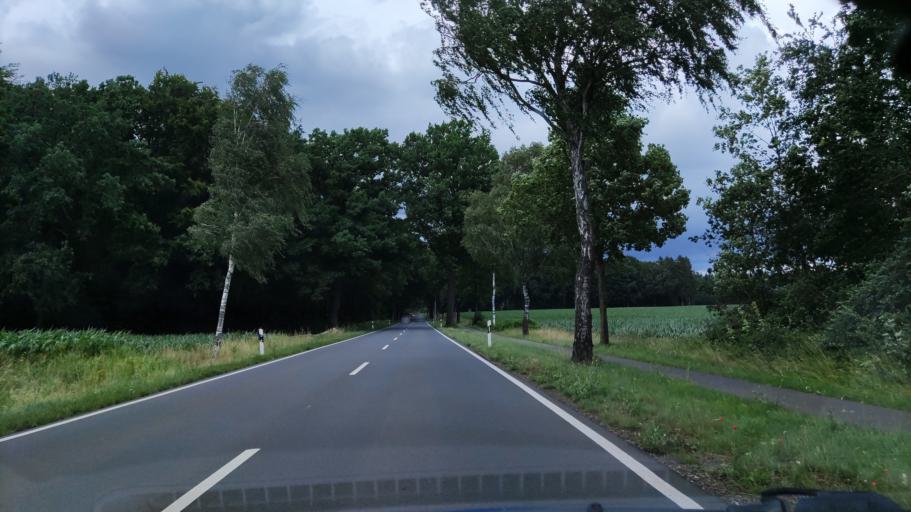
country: DE
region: Lower Saxony
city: Soltau
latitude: 52.9430
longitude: 9.7925
